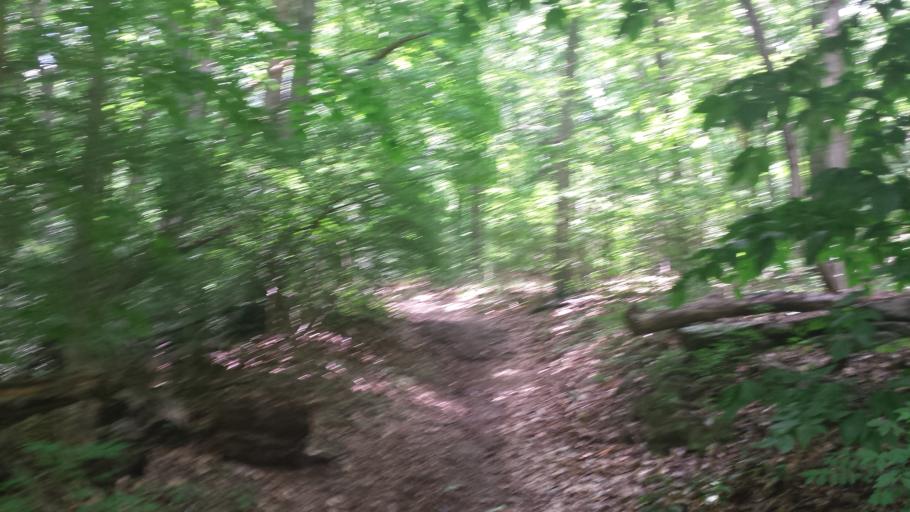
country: US
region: New York
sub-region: Westchester County
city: Scarsdale
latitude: 40.9920
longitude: -73.7524
